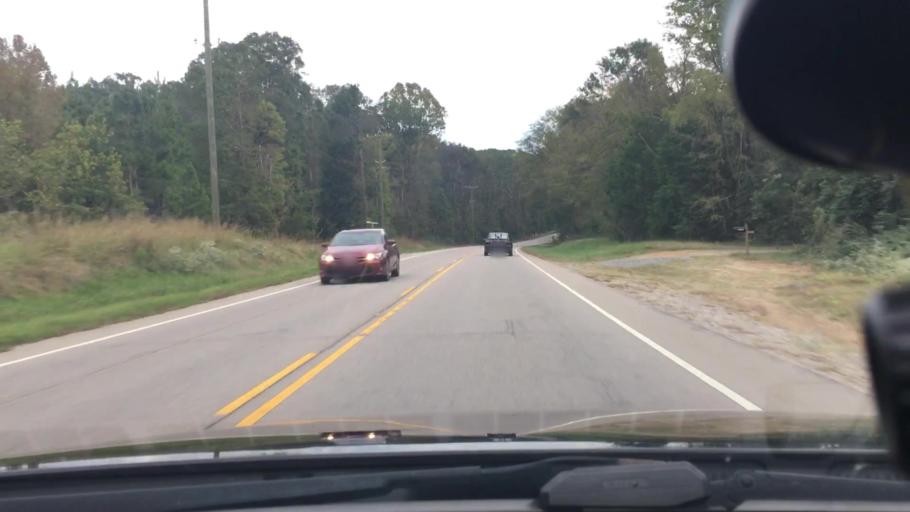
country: US
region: North Carolina
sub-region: Moore County
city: Robbins
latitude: 35.4043
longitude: -79.5703
